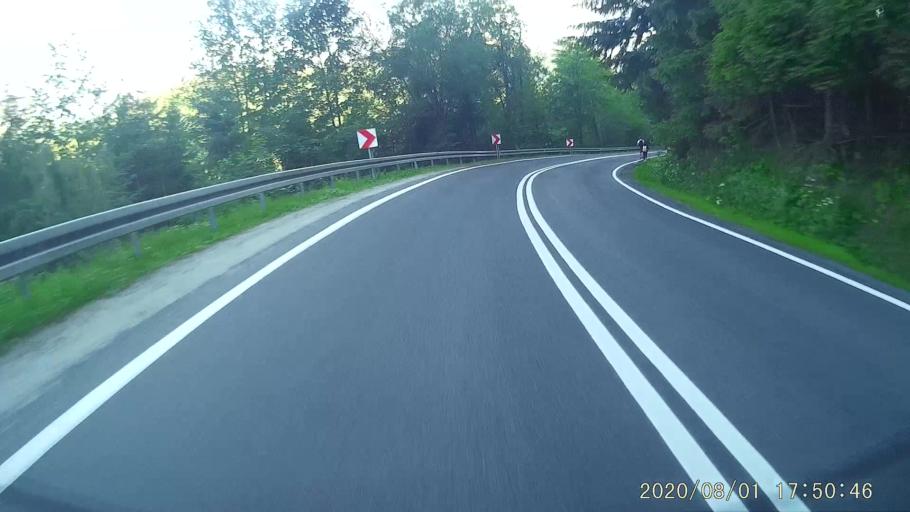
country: PL
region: Lesser Poland Voivodeship
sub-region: Powiat tatrzanski
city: Bukowina Tatrzanska
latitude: 49.2732
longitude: 20.1209
